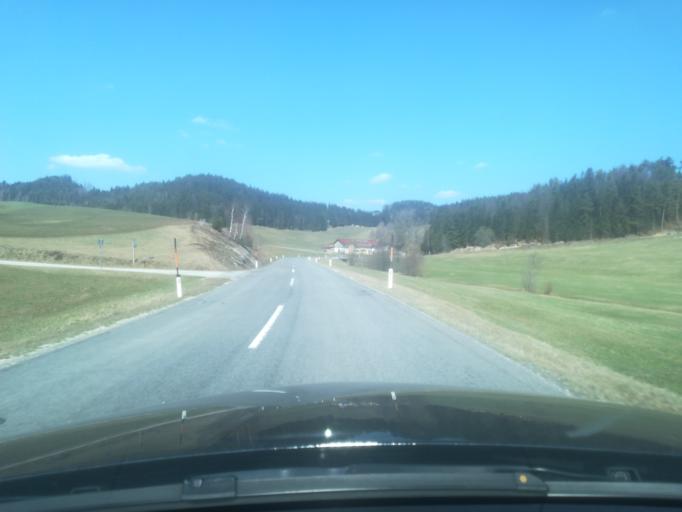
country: AT
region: Lower Austria
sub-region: Politischer Bezirk Zwettl
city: Langschlag
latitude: 48.4912
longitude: 14.8124
